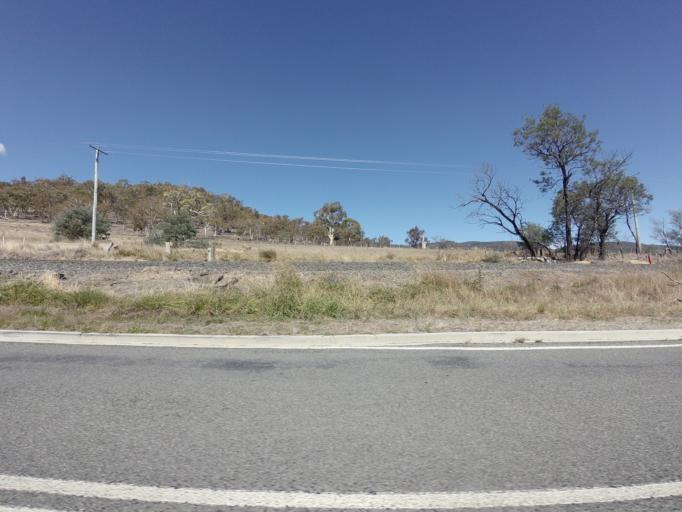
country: AU
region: Tasmania
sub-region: Northern Midlands
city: Evandale
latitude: -41.7384
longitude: 147.8049
